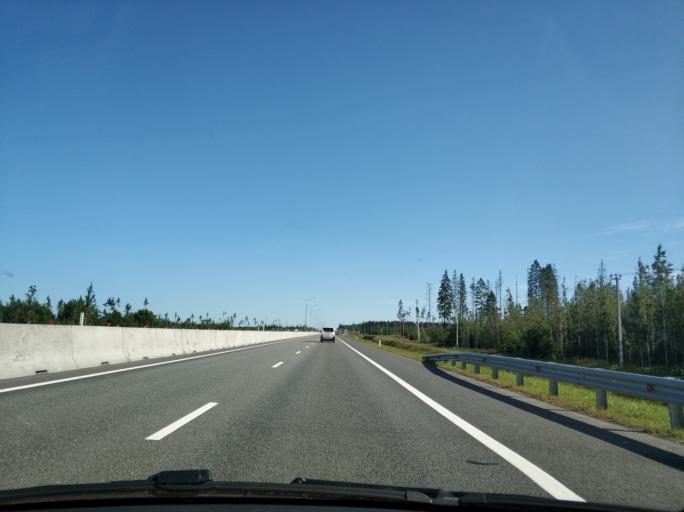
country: RU
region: Leningrad
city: Sosnovo
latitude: 60.4708
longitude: 30.1960
